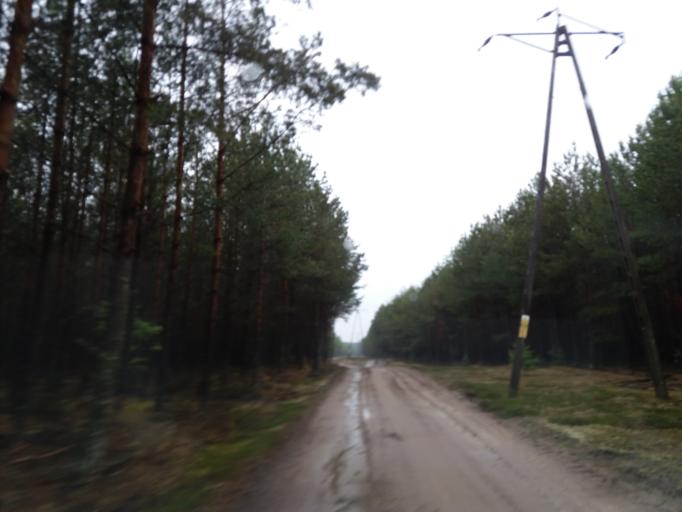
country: PL
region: West Pomeranian Voivodeship
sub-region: Powiat drawski
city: Kalisz Pomorski
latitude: 53.1788
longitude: 15.9753
